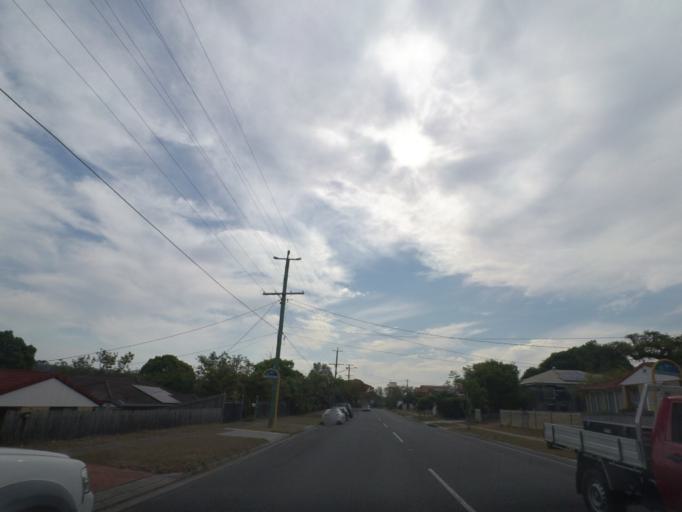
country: AU
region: Queensland
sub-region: Brisbane
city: Inala
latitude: -27.5909
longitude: 152.9660
